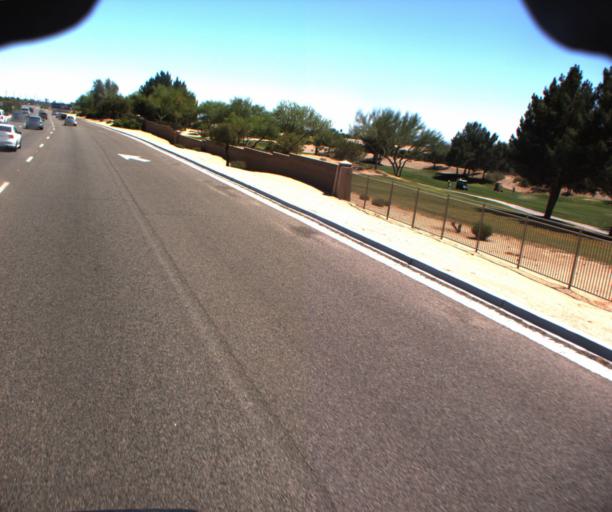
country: US
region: Arizona
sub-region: Maricopa County
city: Sun City West
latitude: 33.6684
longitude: -112.3896
